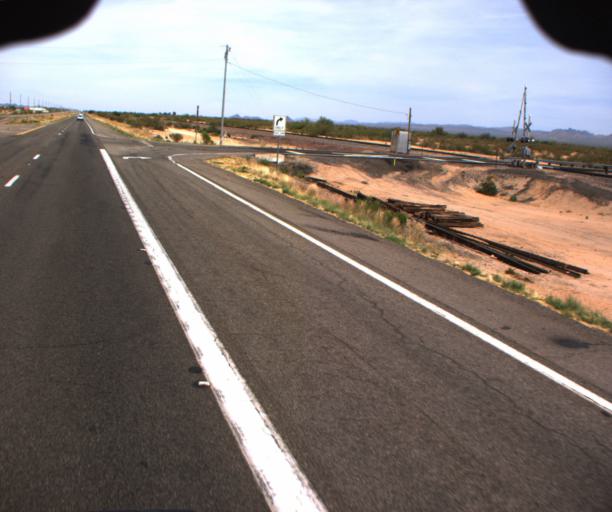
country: US
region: Arizona
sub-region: Maricopa County
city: Sun City West
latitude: 33.7557
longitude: -112.5000
